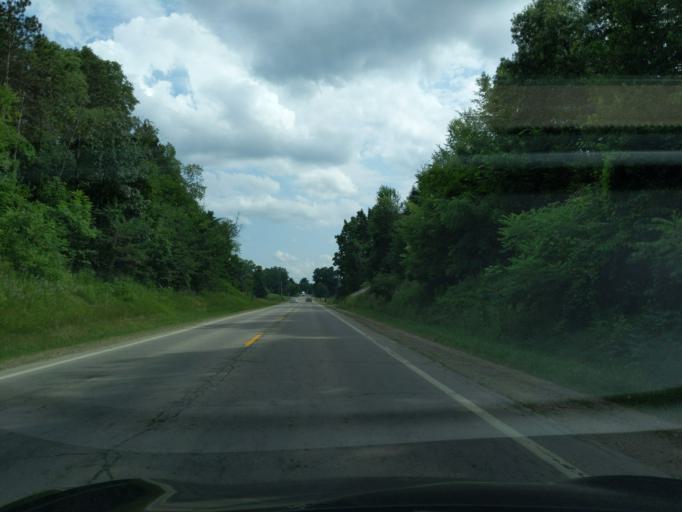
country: US
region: Michigan
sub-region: Eaton County
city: Eaton Rapids
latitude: 42.4883
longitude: -84.6596
